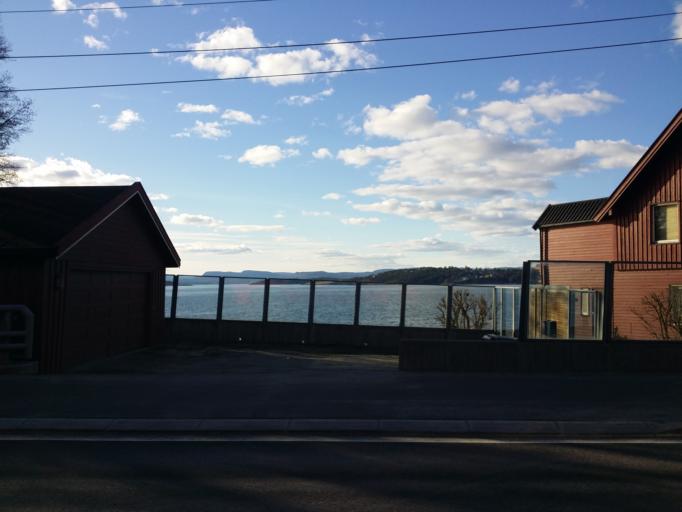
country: NO
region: Akershus
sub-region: Oppegard
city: Kolbotn
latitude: 59.8489
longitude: 10.7801
